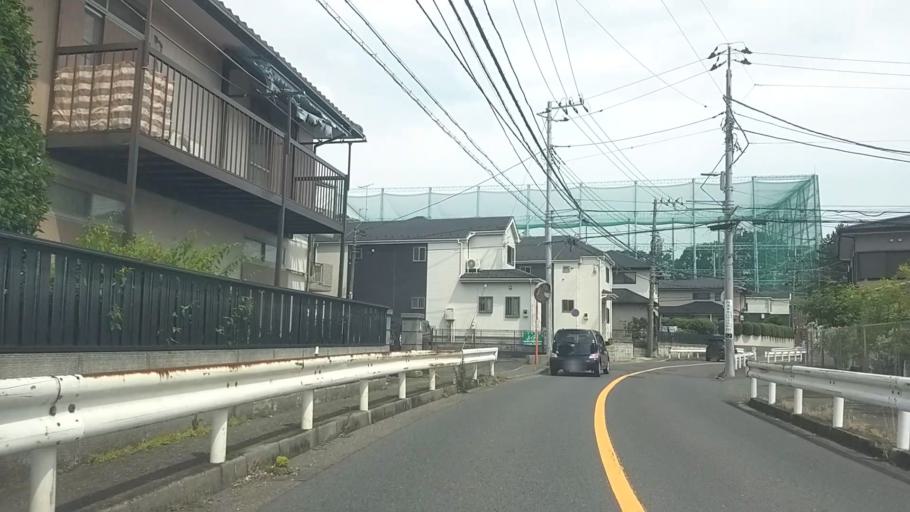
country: JP
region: Kanagawa
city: Fujisawa
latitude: 35.3896
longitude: 139.4621
